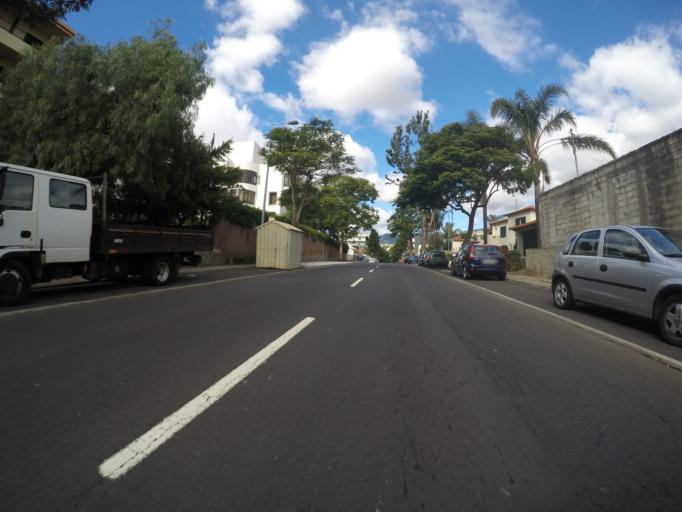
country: PT
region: Madeira
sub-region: Funchal
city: Nossa Senhora do Monte
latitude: 32.6574
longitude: -16.9262
